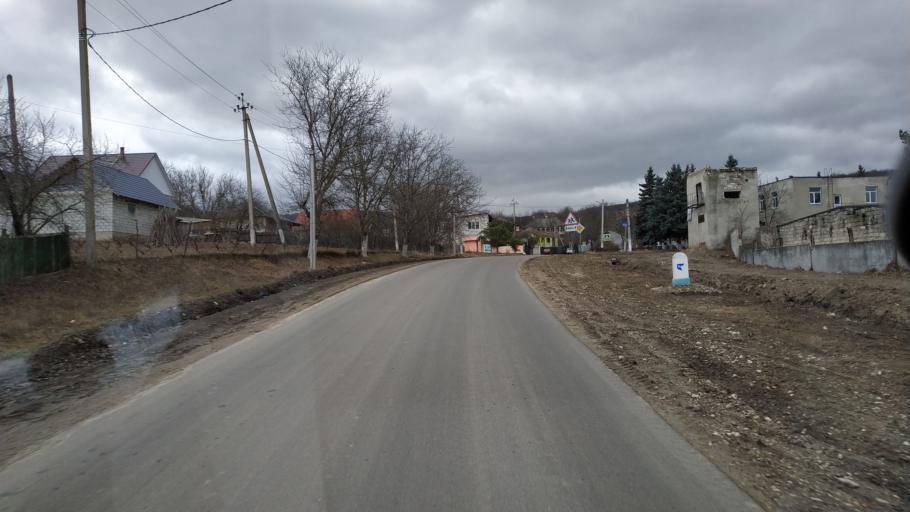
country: MD
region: Calarasi
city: Calarasi
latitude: 47.2456
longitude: 28.2860
